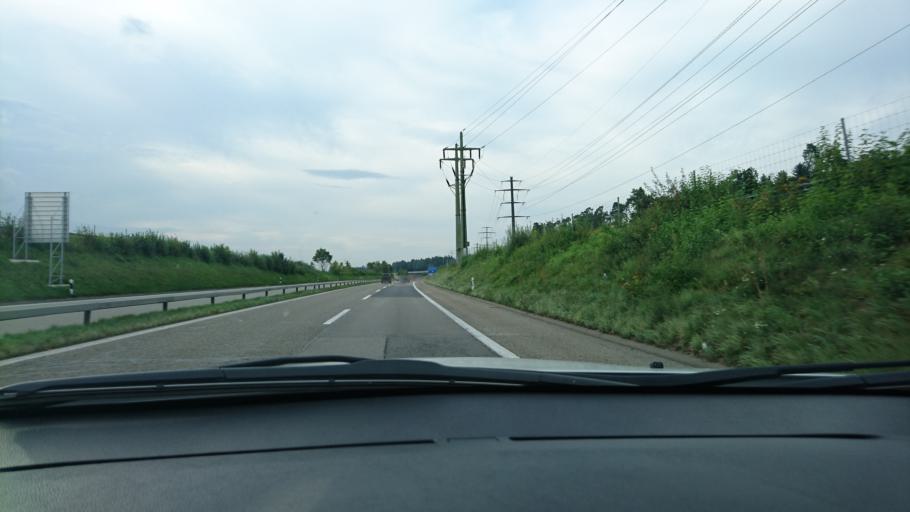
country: CH
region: Zurich
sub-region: Bezirk Uster
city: Uster / Gschwader
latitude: 47.3652
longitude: 8.7182
